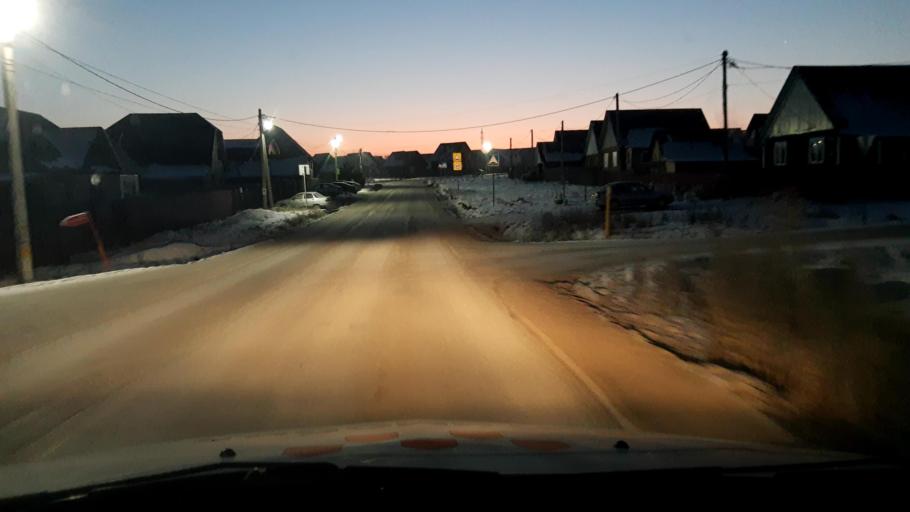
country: RU
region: Bashkortostan
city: Iglino
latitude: 54.8291
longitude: 56.4339
